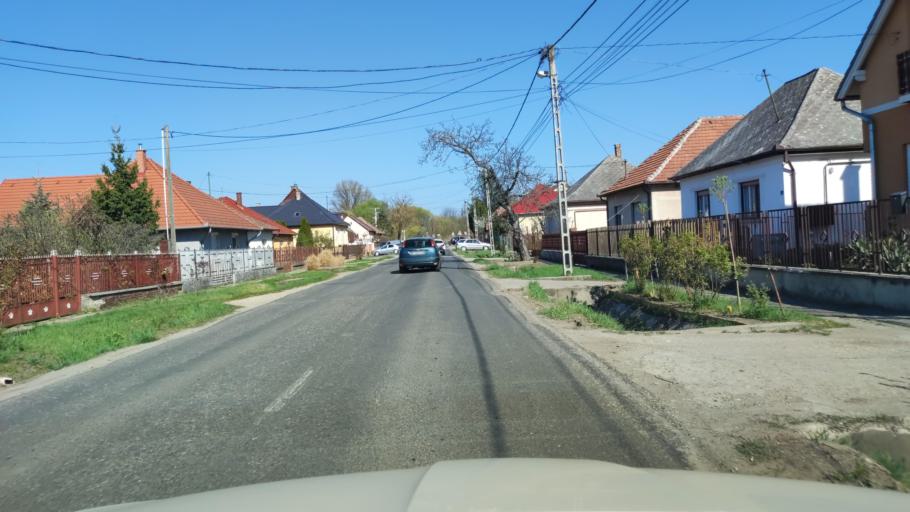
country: HU
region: Pest
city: Nagytarcsa
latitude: 47.5332
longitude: 19.2799
